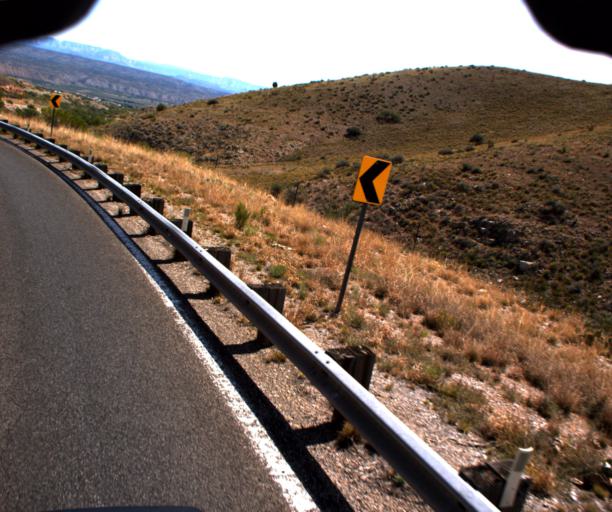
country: US
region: Arizona
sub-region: Yavapai County
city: Clarkdale
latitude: 34.7541
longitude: -112.0927
